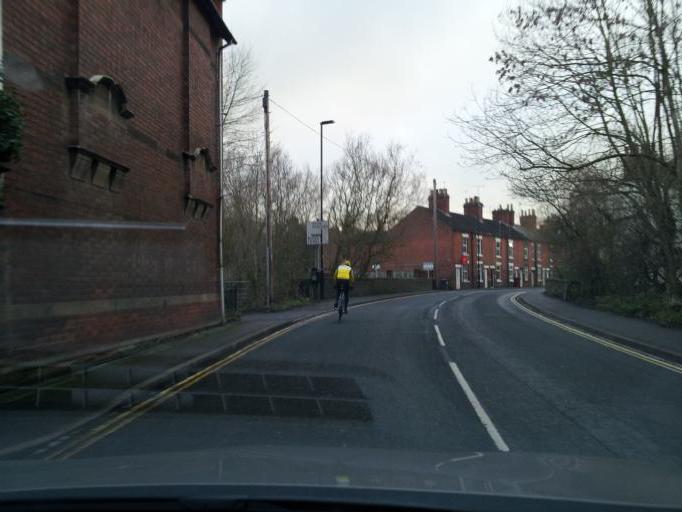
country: GB
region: England
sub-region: Staffordshire
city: Burton upon Trent
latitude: 52.8600
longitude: -1.6835
